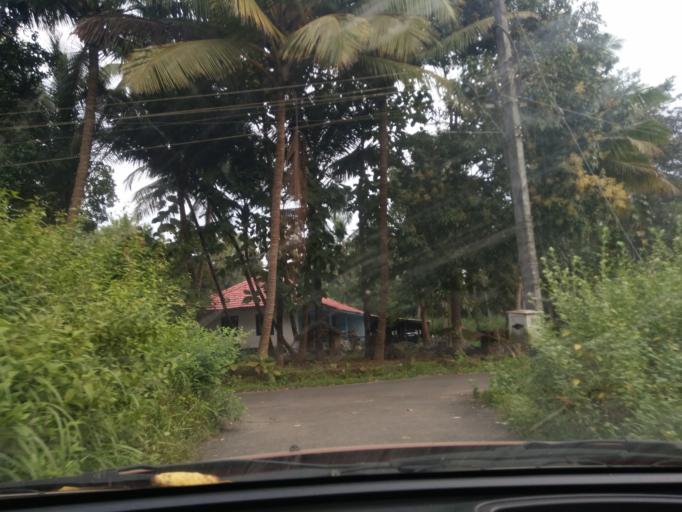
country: IN
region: Goa
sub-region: South Goa
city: Varca
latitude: 15.2302
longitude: 73.9515
